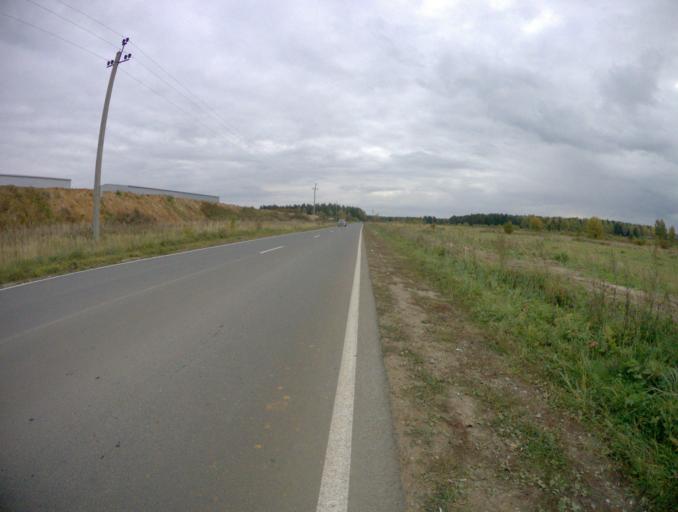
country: RU
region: Vladimir
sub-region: Kovrovskiy Rayon
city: Kovrov
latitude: 56.3714
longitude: 41.3709
